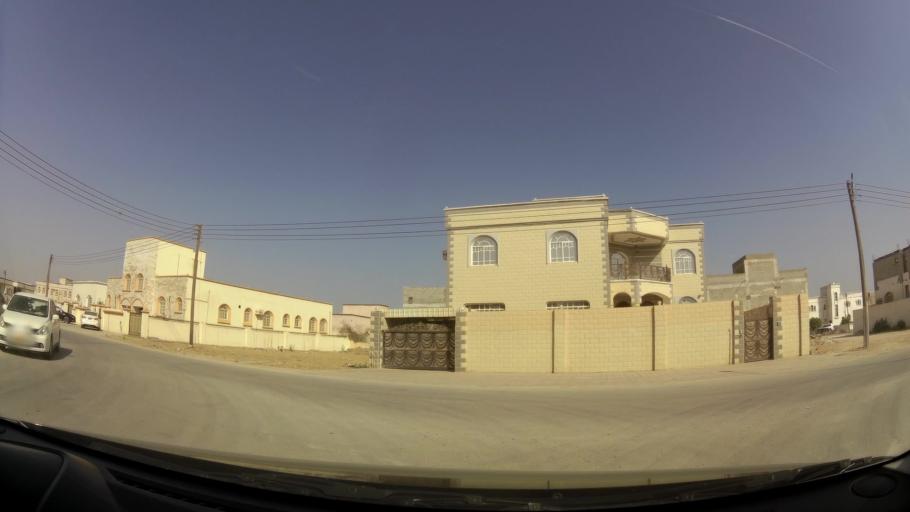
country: OM
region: Zufar
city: Salalah
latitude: 17.0139
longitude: 54.0111
